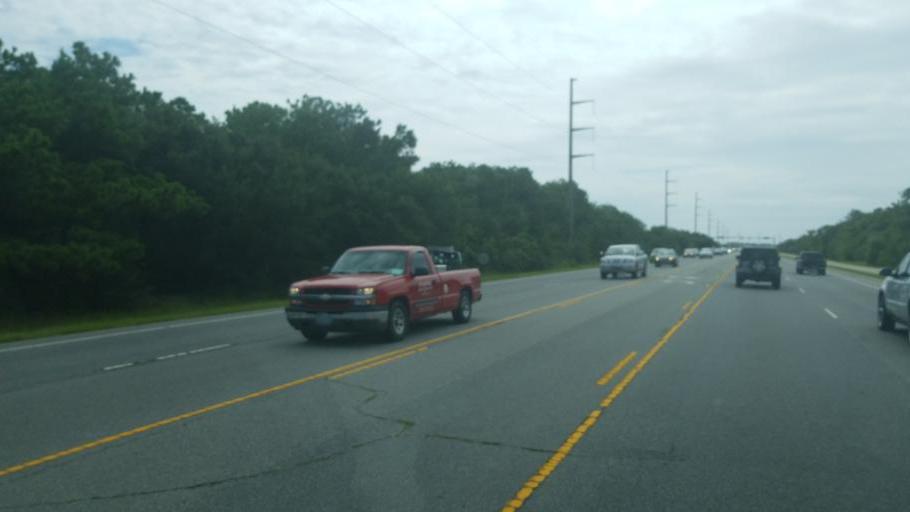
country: US
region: North Carolina
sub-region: Dare County
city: Nags Head
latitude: 35.9694
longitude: -75.6350
